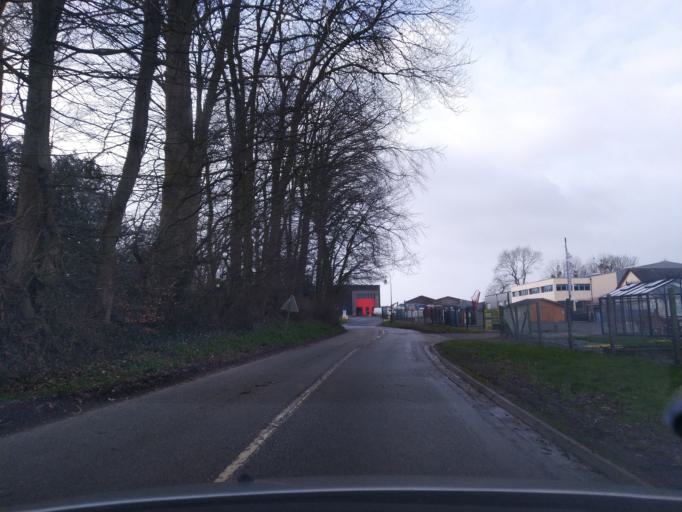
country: FR
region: Haute-Normandie
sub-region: Departement de la Seine-Maritime
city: Pissy-Poville
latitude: 49.5198
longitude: 0.9884
